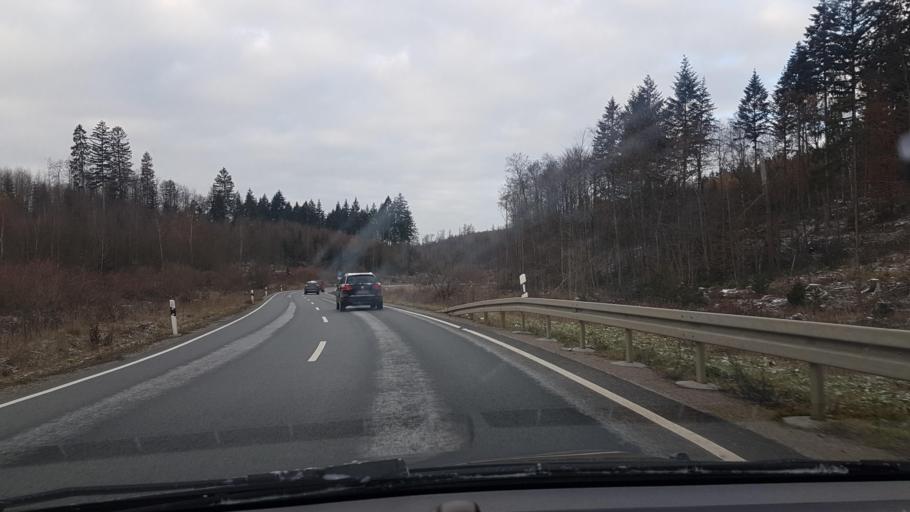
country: DE
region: Lower Saxony
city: Bad Grund
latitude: 51.8265
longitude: 10.2160
